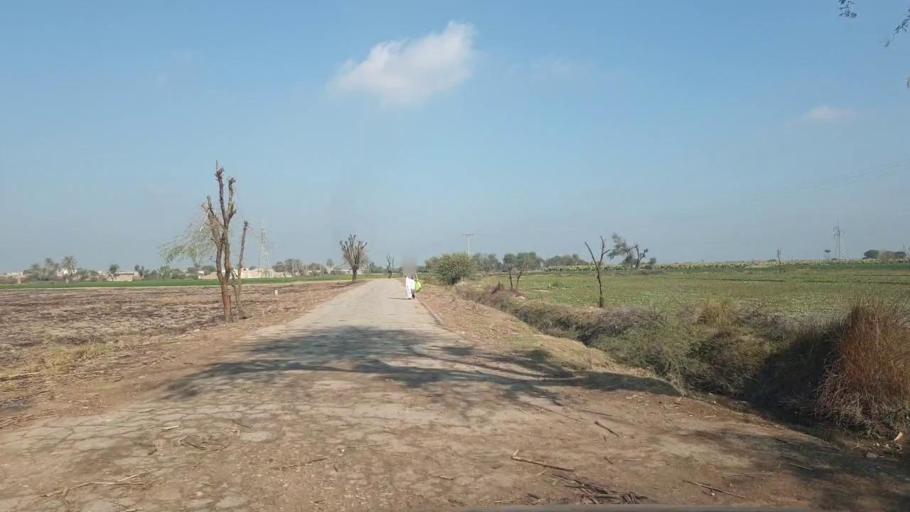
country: PK
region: Sindh
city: Shahdadpur
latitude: 25.8849
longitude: 68.5651
